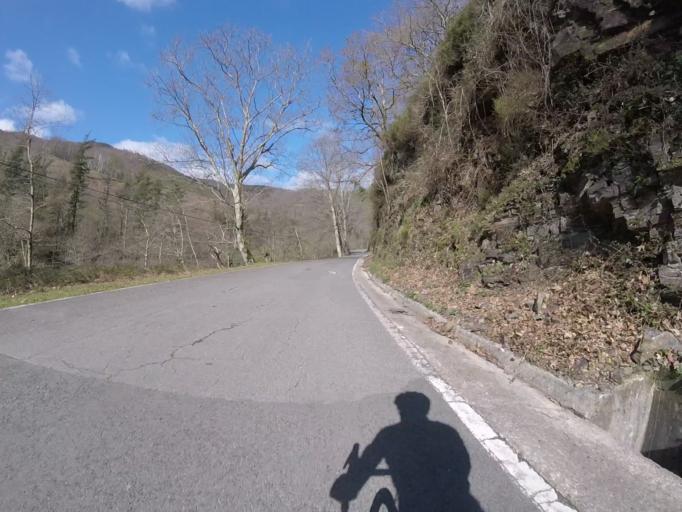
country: ES
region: Navarre
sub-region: Provincia de Navarra
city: Goizueta
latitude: 43.1435
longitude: -1.8493
